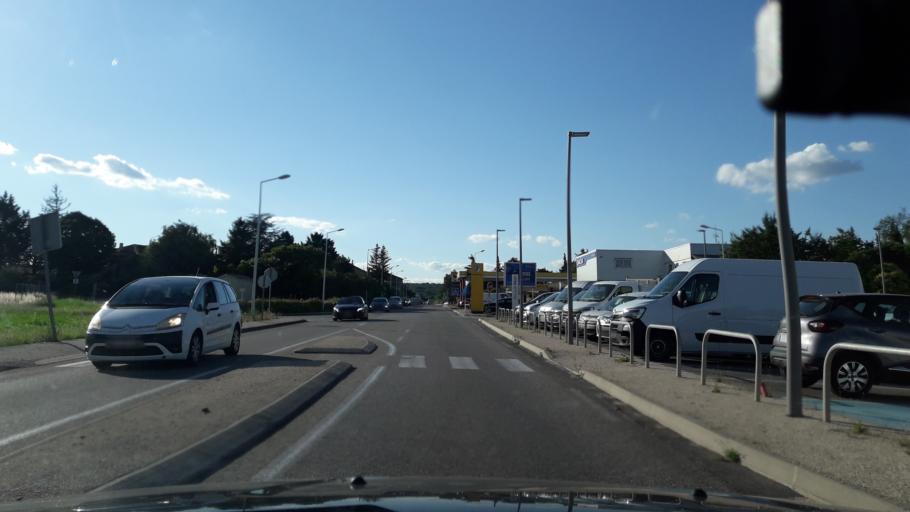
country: FR
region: Rhone-Alpes
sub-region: Departement de l'Ardeche
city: Lavilledieu
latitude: 44.5699
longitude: 4.4598
